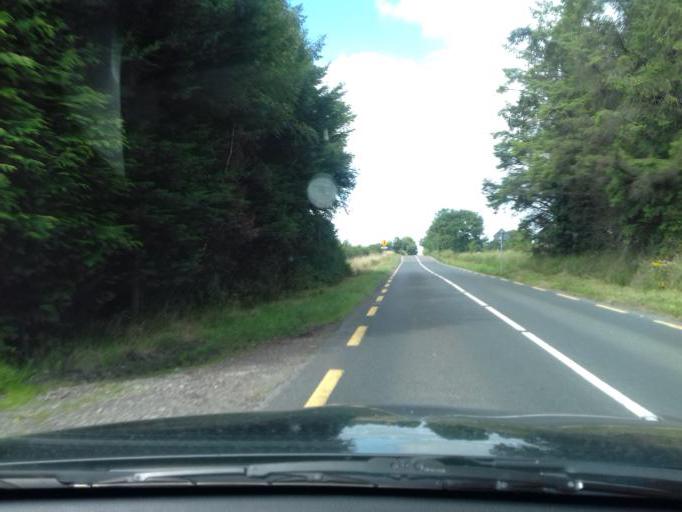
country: IE
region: Leinster
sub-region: Wicklow
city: Baltinglass
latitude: 52.9864
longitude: -6.6559
